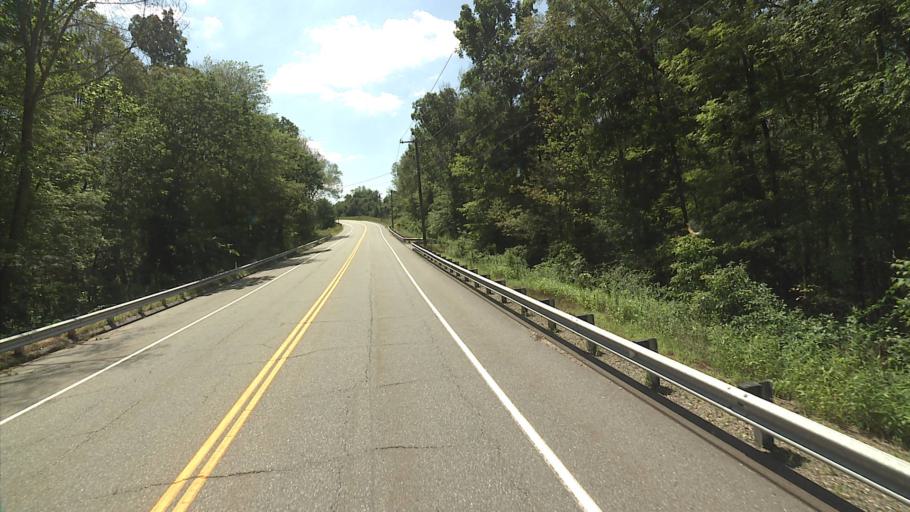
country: US
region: Connecticut
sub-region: Windham County
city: Plainfield Village
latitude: 41.6907
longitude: -71.9534
